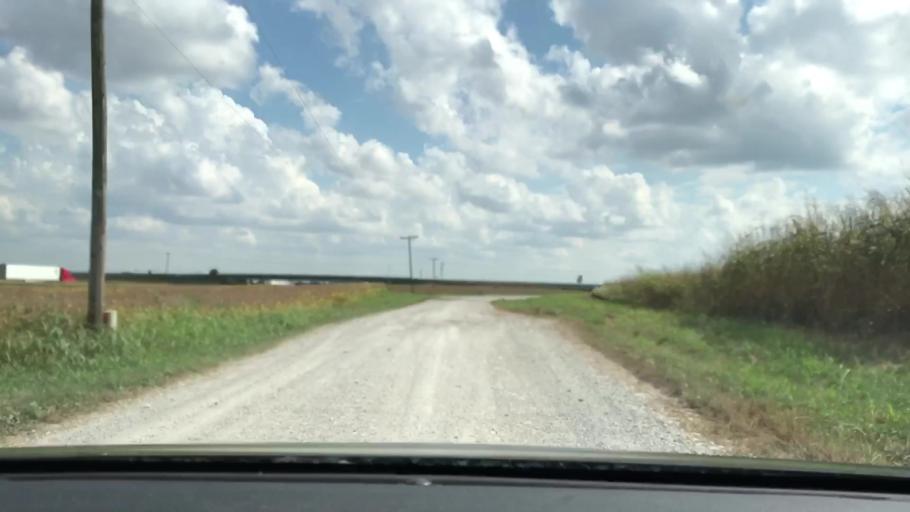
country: US
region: Kentucky
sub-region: Christian County
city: Oak Grove
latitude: 36.6824
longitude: -87.4087
